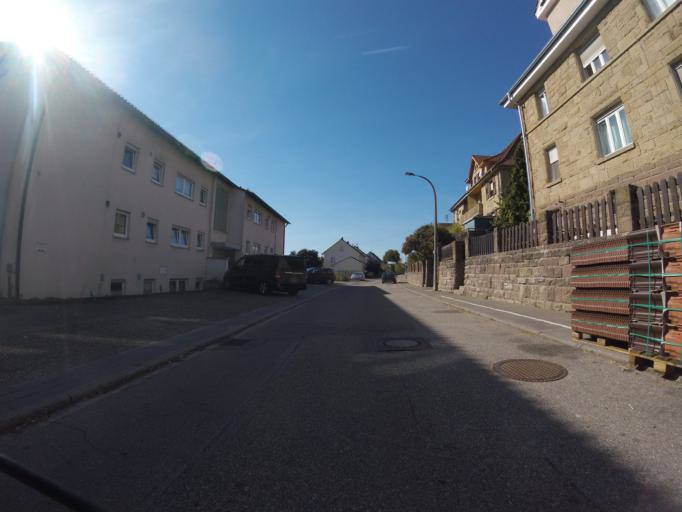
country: DE
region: Baden-Wuerttemberg
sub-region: Karlsruhe Region
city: Maulbronn
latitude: 48.9990
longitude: 8.8003
